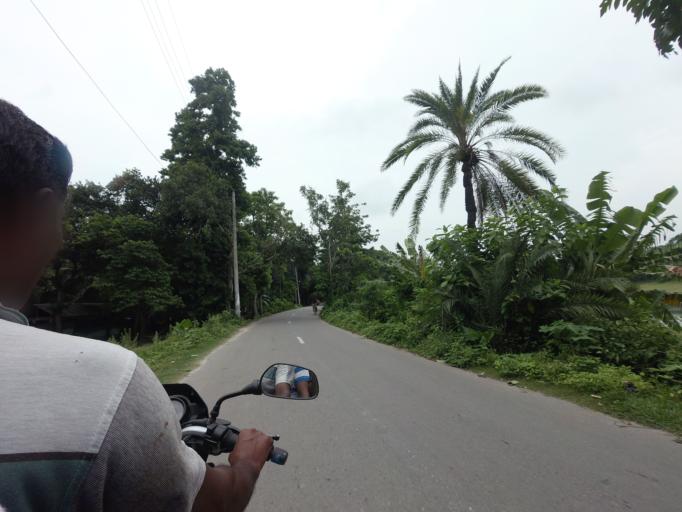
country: BD
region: Khulna
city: Kalia
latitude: 23.1750
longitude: 89.6468
